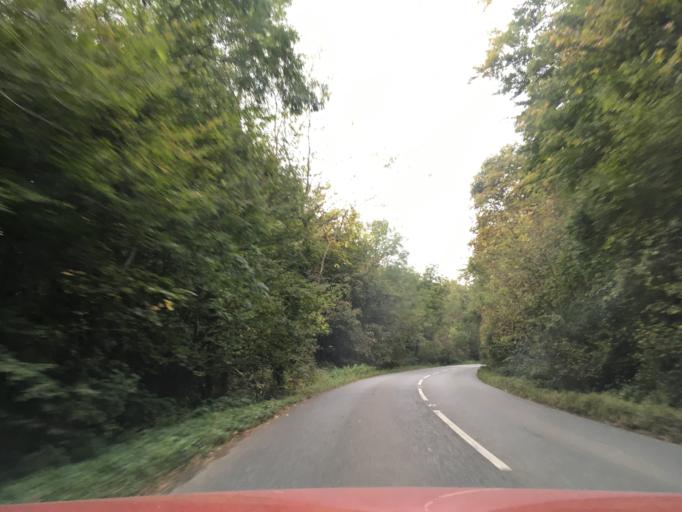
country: GB
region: England
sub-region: Gloucestershire
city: Dursley
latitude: 51.6698
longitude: -2.3297
